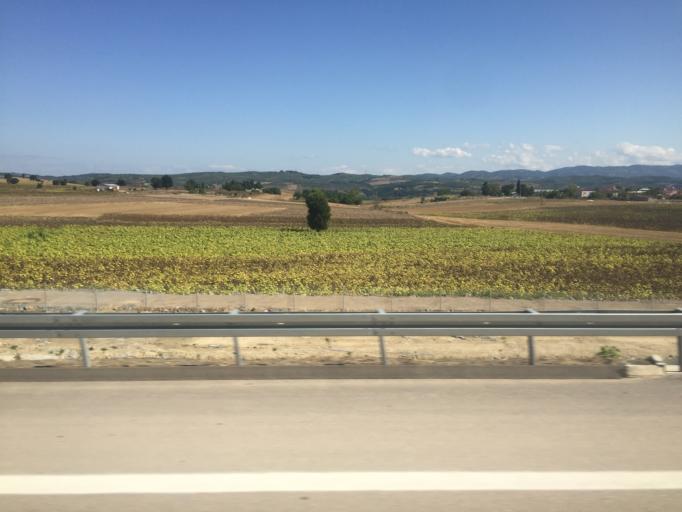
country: TR
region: Bursa
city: Mahmudiye
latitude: 40.2578
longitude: 28.6914
